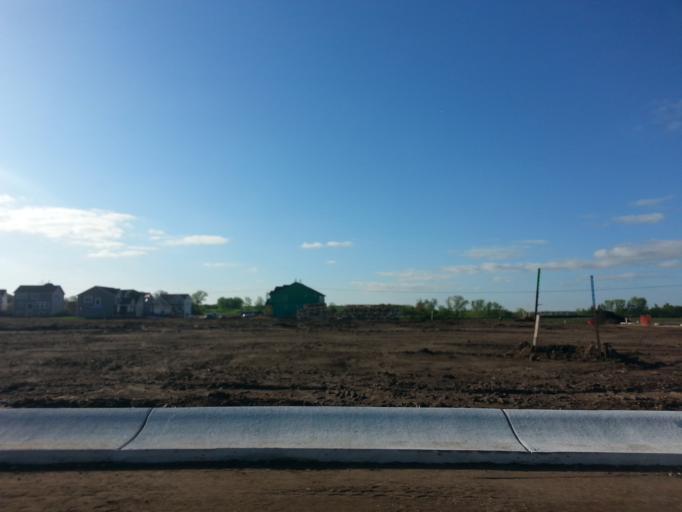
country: US
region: Minnesota
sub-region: Washington County
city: Lake Elmo
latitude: 44.9541
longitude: -92.9044
